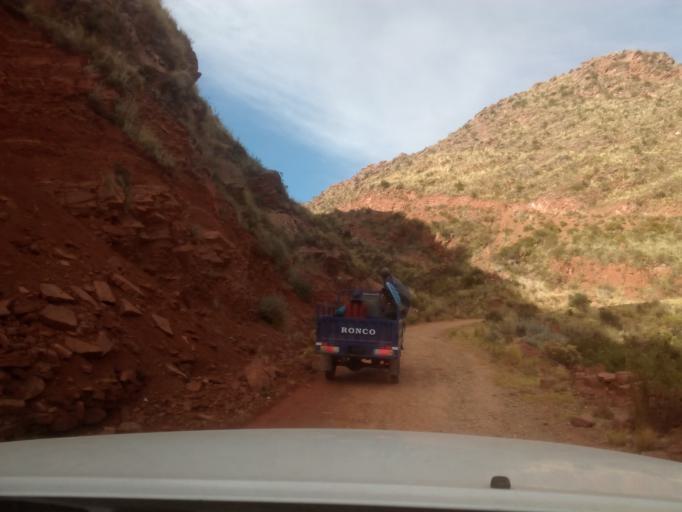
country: PE
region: Puno
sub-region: El Collao
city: Ilave
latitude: -15.9756
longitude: -69.6780
